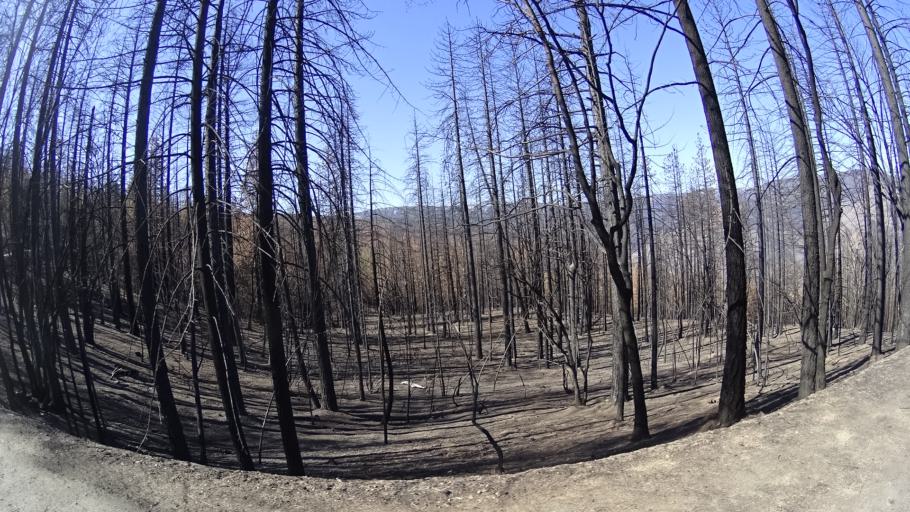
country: US
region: California
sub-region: Tehama County
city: Rancho Tehama Reserve
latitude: 39.6755
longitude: -122.7089
